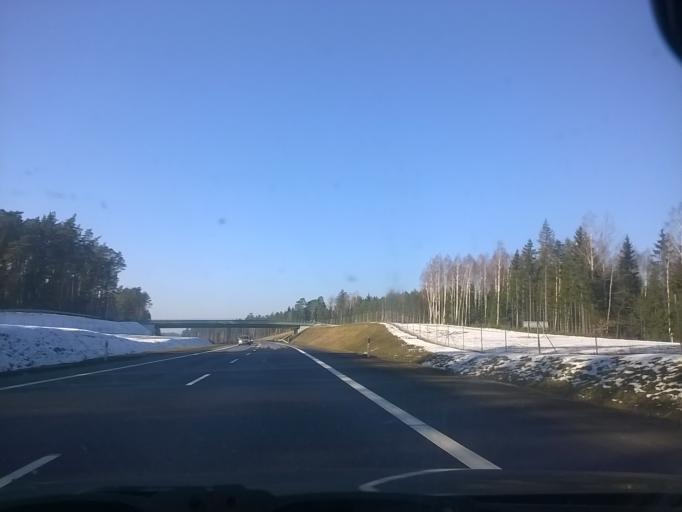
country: PL
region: Warmian-Masurian Voivodeship
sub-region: Powiat olsztynski
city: Barczewo
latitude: 53.8371
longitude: 20.7633
